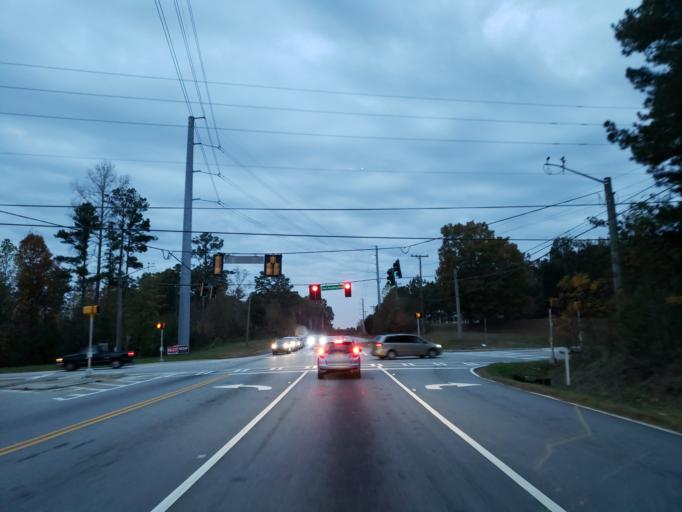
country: US
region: Georgia
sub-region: Paulding County
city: Hiram
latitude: 33.9418
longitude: -84.7379
